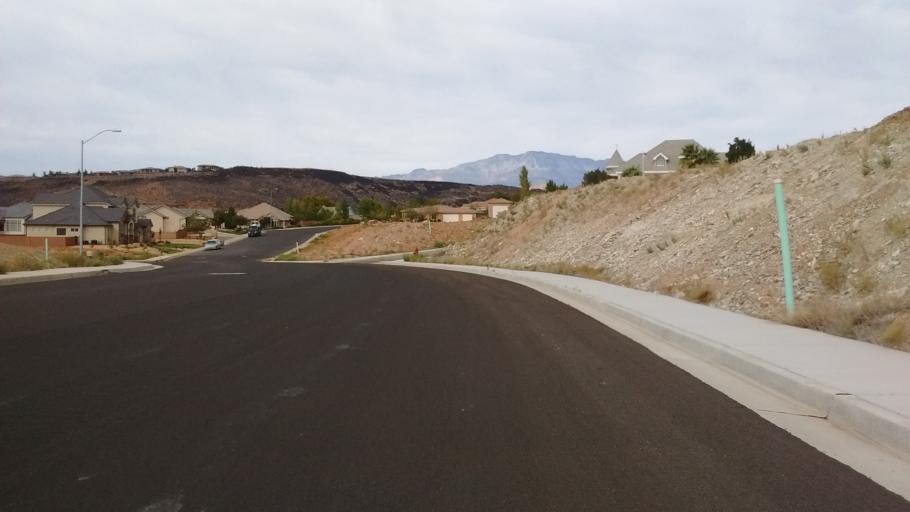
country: US
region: Utah
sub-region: Washington County
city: Washington
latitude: 37.1162
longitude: -113.4944
